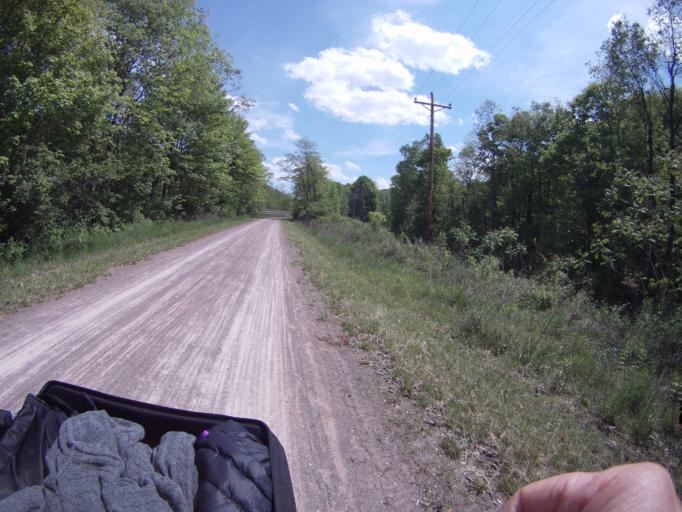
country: US
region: Pennsylvania
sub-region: Somerset County
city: Meyersdale
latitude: 39.8046
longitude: -78.9850
